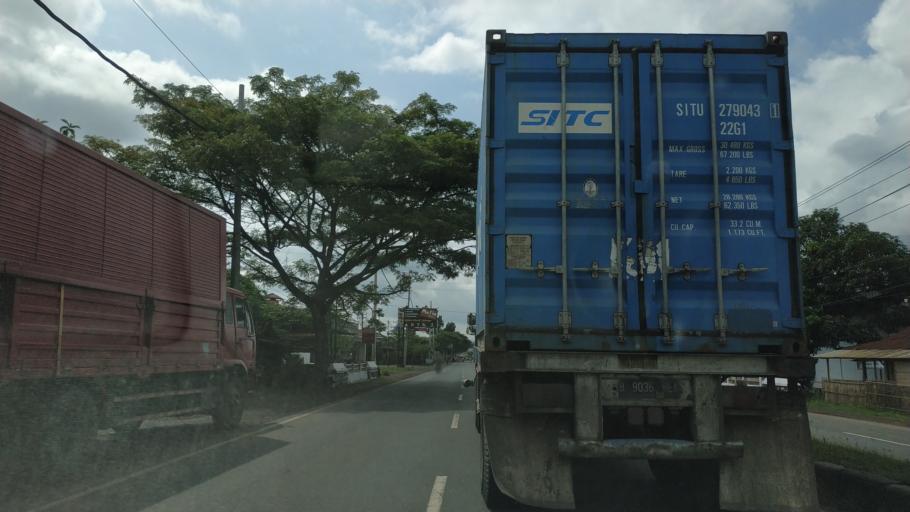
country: ID
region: Central Java
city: Pekalongan
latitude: -6.9509
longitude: 109.7973
